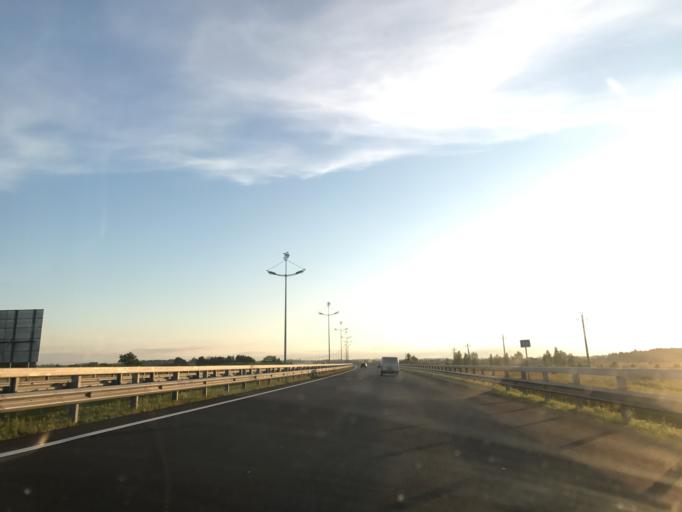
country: RU
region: Kaliningrad
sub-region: Zelenogradskiy Rayon
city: Zelenogradsk
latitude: 54.9238
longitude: 20.3888
